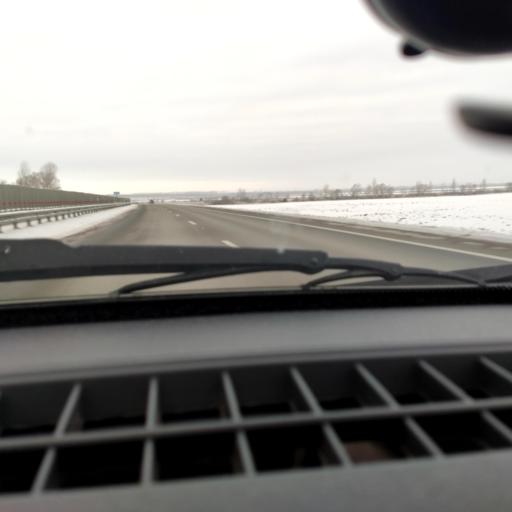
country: RU
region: Bashkortostan
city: Kushnarenkovo
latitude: 55.0655
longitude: 55.3655
